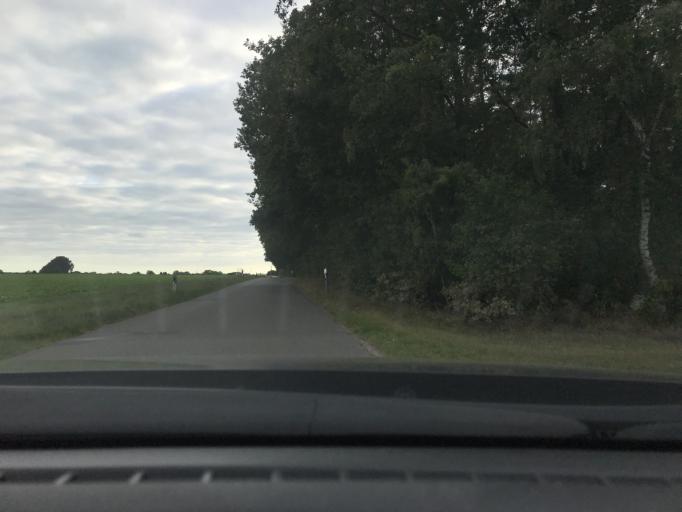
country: DE
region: Lower Saxony
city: Suderburg
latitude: 52.9107
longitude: 10.4560
